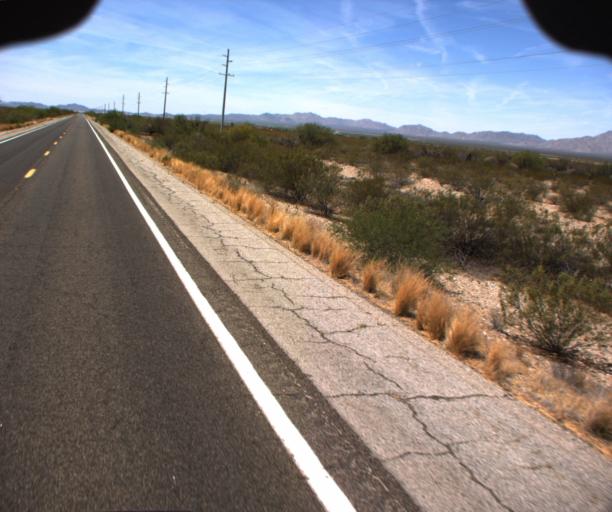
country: US
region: Arizona
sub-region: La Paz County
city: Salome
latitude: 33.8481
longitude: -113.4572
